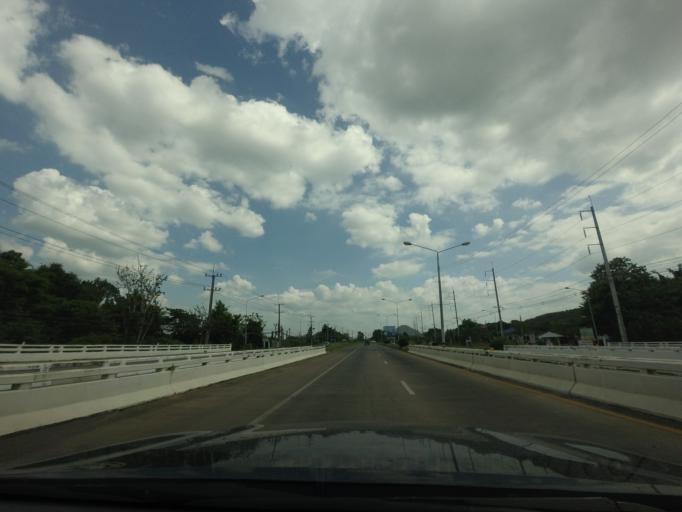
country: TH
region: Phetchabun
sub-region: Amphoe Bueng Sam Phan
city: Bueng Sam Phan
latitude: 15.7705
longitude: 101.0086
